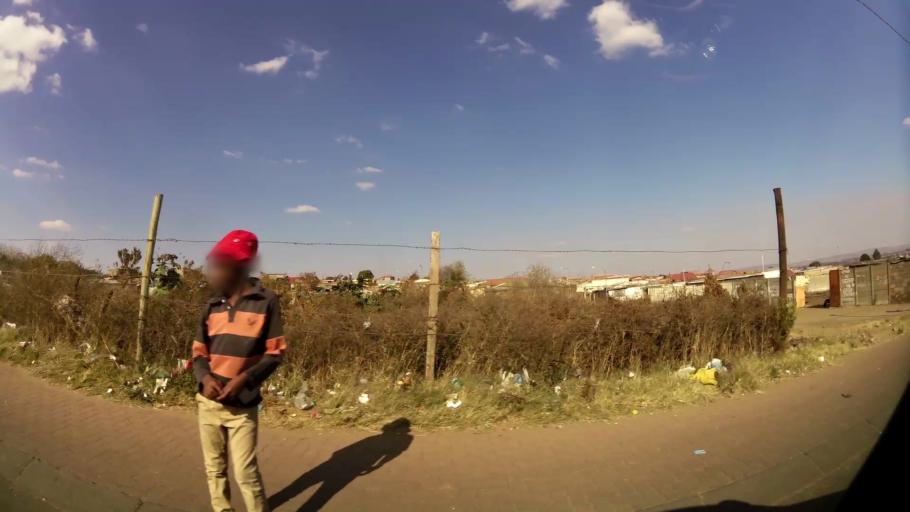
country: ZA
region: Gauteng
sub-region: City of Johannesburg Metropolitan Municipality
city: Soweto
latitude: -26.2231
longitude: 27.8882
